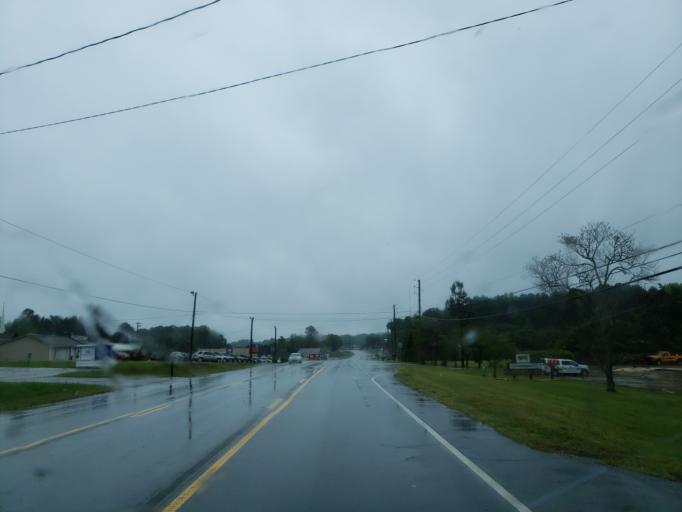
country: US
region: Georgia
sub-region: Carroll County
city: Villa Rica
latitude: 33.7316
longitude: -84.9474
